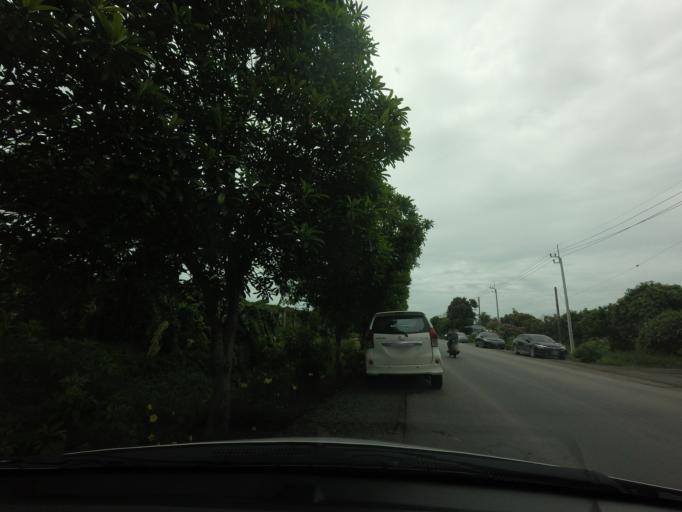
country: TH
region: Bangkok
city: Nong Chok
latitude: 13.8721
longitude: 100.8085
